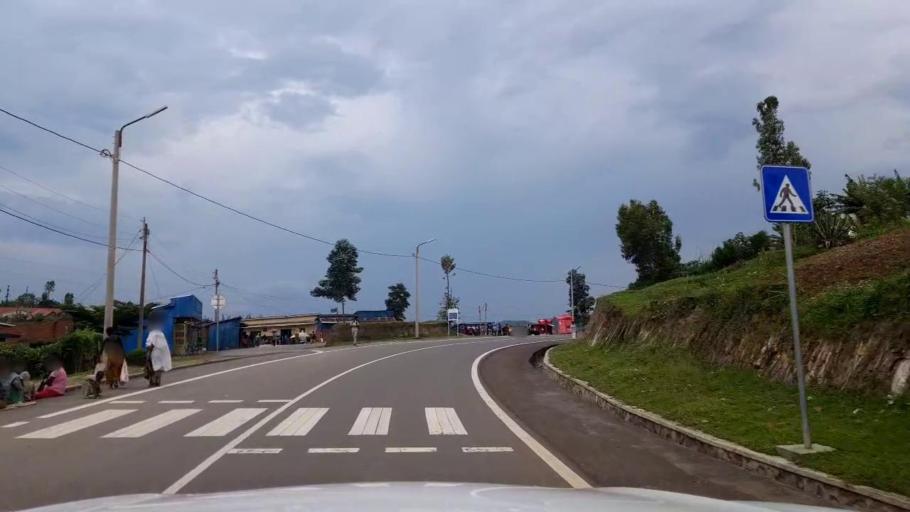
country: RW
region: Western Province
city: Kibuye
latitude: -2.0415
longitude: 29.4048
